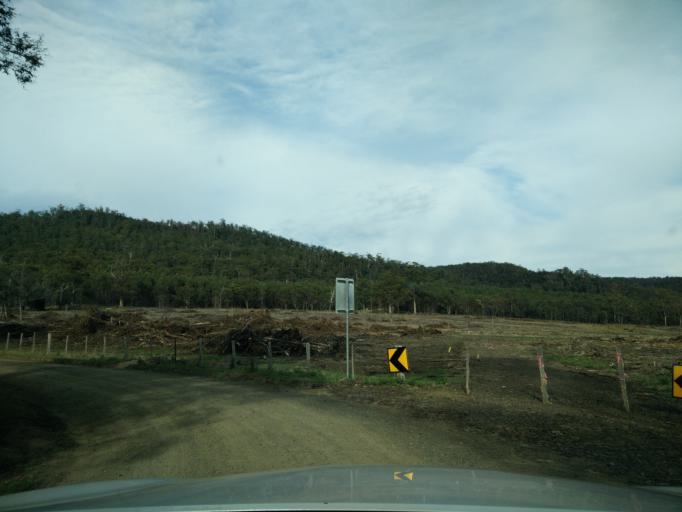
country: AU
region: Tasmania
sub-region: Break O'Day
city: St Helens
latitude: -41.8701
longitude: 148.1992
